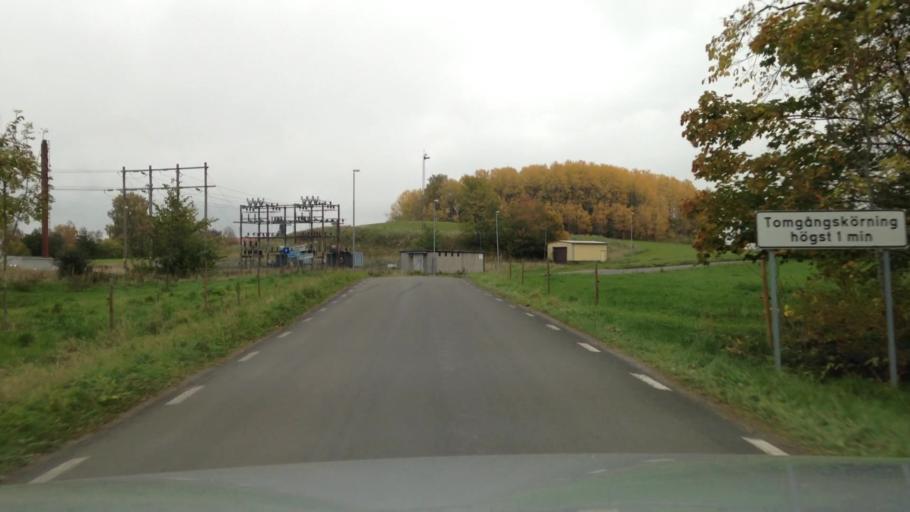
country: SE
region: Vaestra Goetaland
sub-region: Falkopings Kommun
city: Akarp
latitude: 58.2708
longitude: 13.7037
